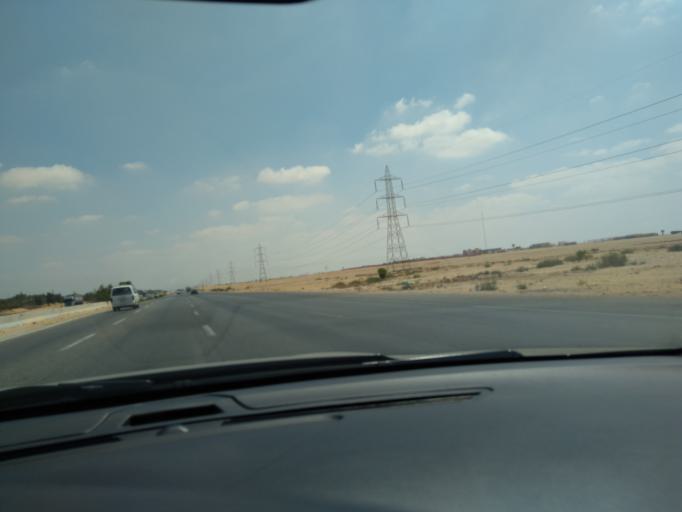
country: EG
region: Al Isma'iliyah
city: At Tall al Kabir
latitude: 30.3871
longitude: 31.9586
